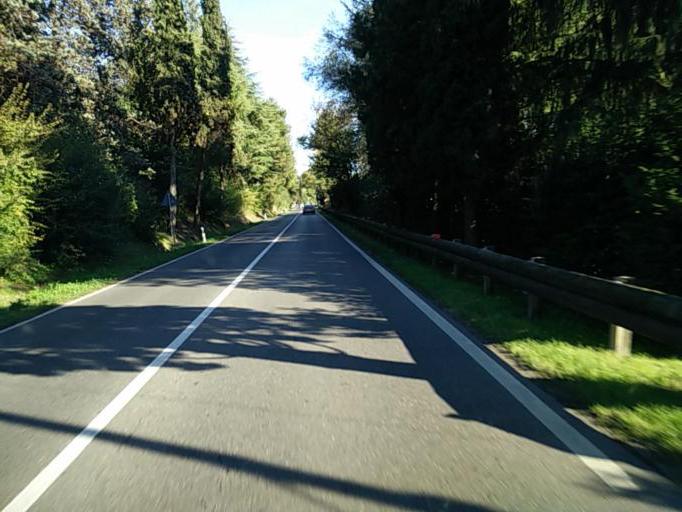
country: IT
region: Lombardy
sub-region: Provincia di Brescia
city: Salo
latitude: 45.6111
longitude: 10.5151
